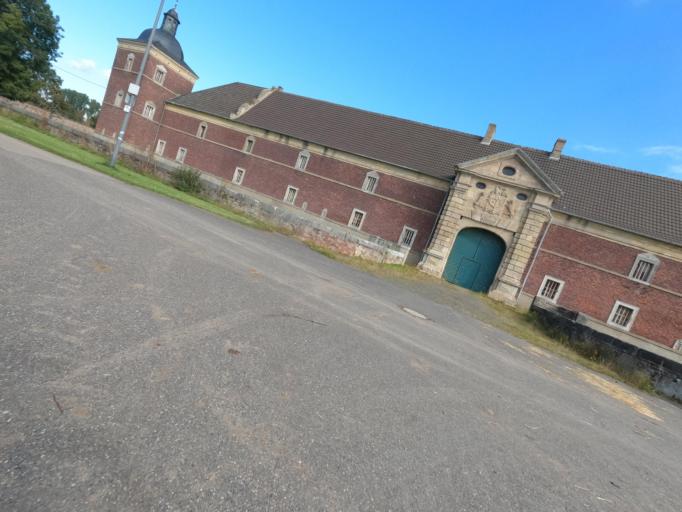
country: DE
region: North Rhine-Westphalia
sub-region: Regierungsbezirk Koln
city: Inden
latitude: 50.8743
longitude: 6.4023
